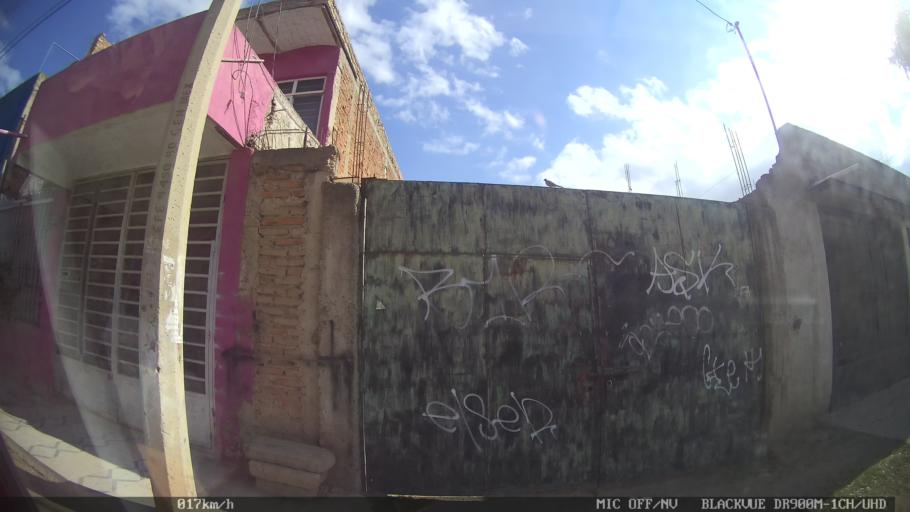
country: MX
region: Jalisco
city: Tonala
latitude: 20.6536
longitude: -103.2442
